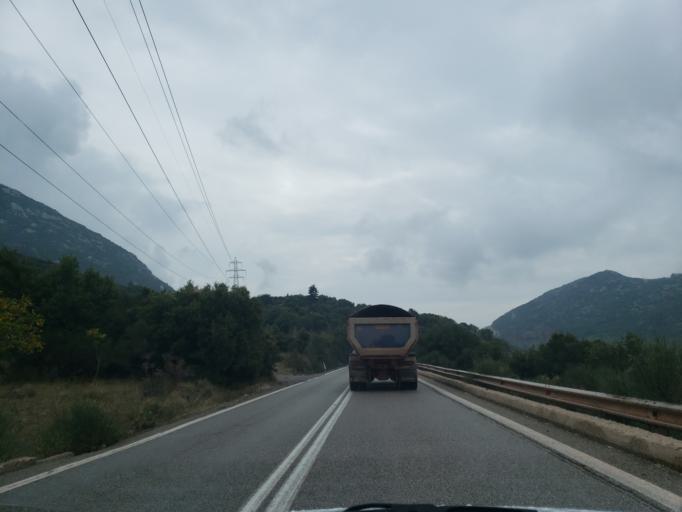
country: GR
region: Central Greece
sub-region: Nomos Fokidos
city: Amfissa
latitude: 38.5767
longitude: 22.3939
